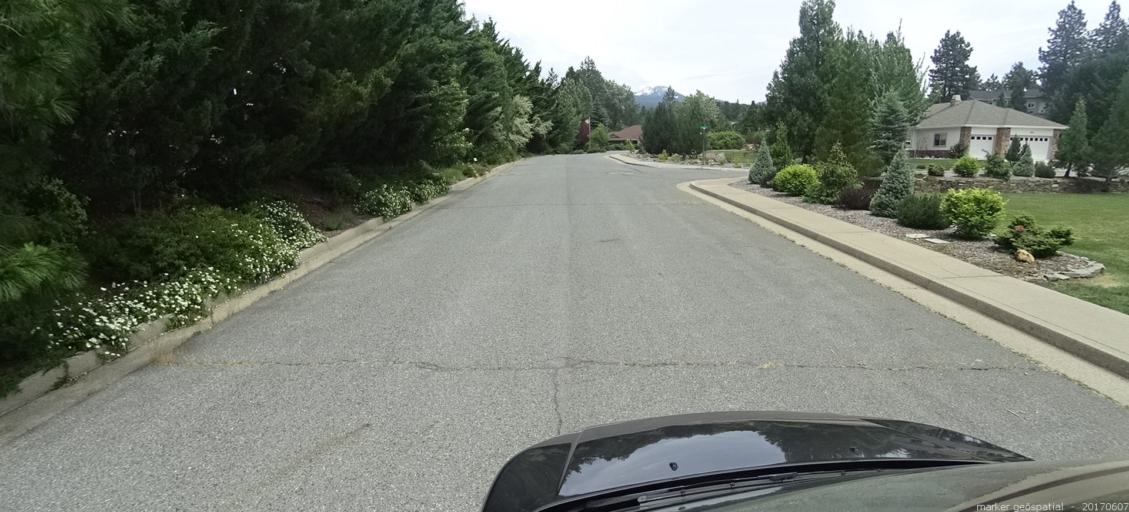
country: US
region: California
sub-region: Siskiyou County
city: Mount Shasta
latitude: 41.2910
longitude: -122.3186
